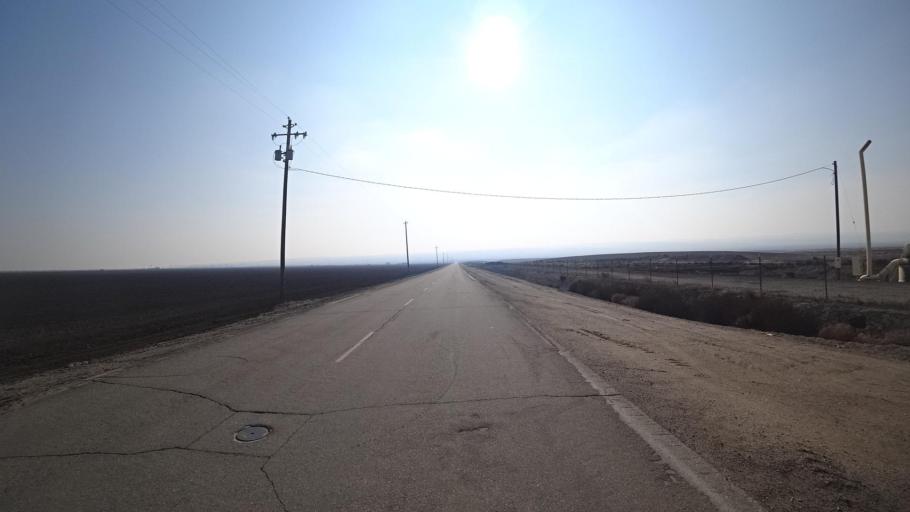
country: US
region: California
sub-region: Kern County
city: Buttonwillow
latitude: 35.3259
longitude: -119.3768
